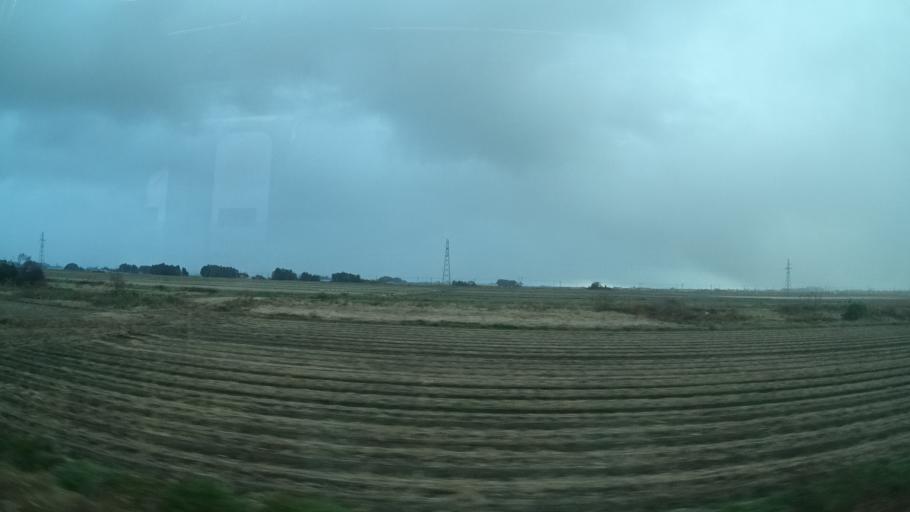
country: JP
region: Miyagi
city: Watari
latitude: 38.0501
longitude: 140.8571
